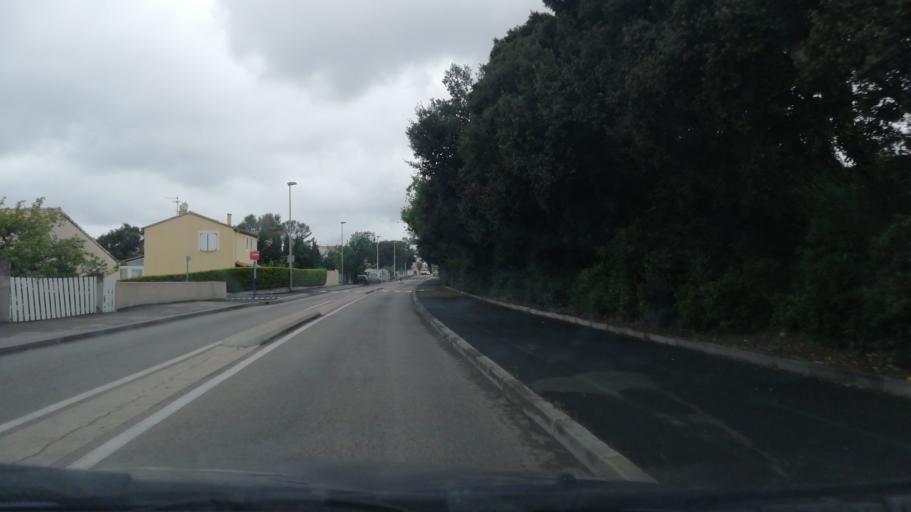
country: FR
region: Languedoc-Roussillon
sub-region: Departement de l'Herault
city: Saint-Gely-du-Fesc
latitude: 43.6873
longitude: 3.8084
